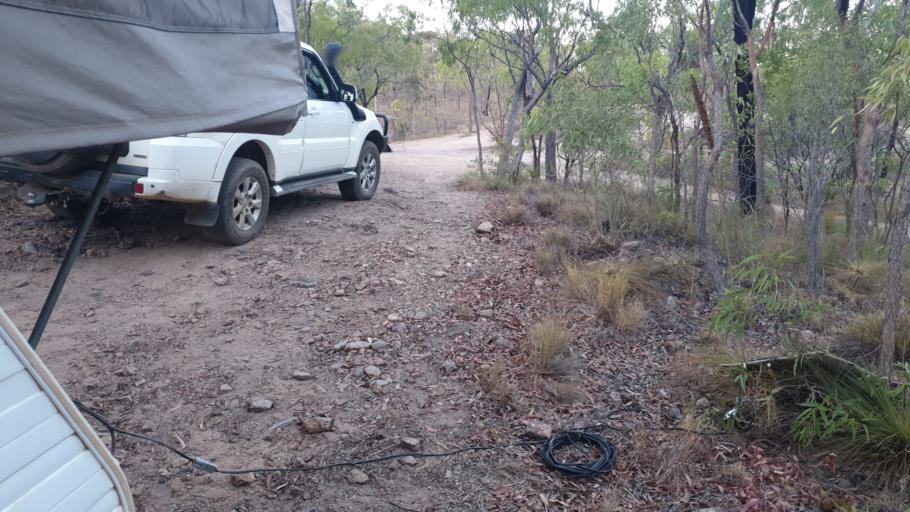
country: AU
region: Queensland
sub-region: Tablelands
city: Atherton
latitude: -17.4048
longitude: 145.2295
